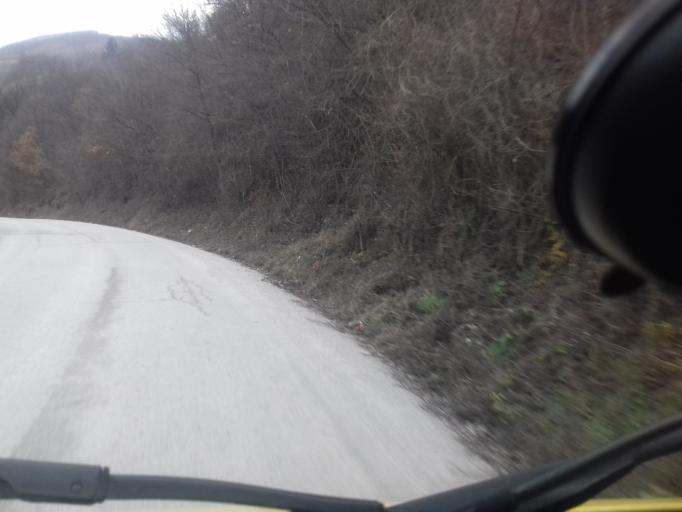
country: BA
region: Federation of Bosnia and Herzegovina
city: Zenica
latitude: 44.2346
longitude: 18.0022
